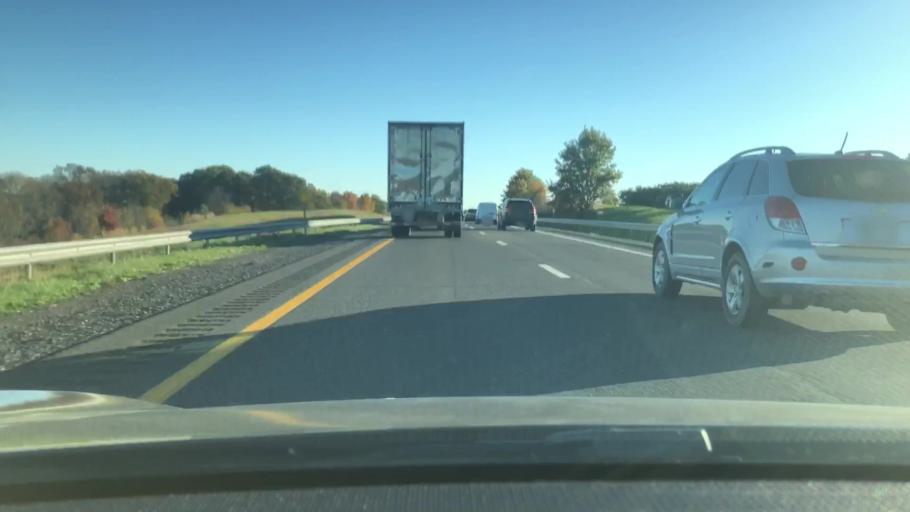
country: US
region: New York
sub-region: Ulster County
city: Plattekill
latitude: 41.6320
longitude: -74.0788
